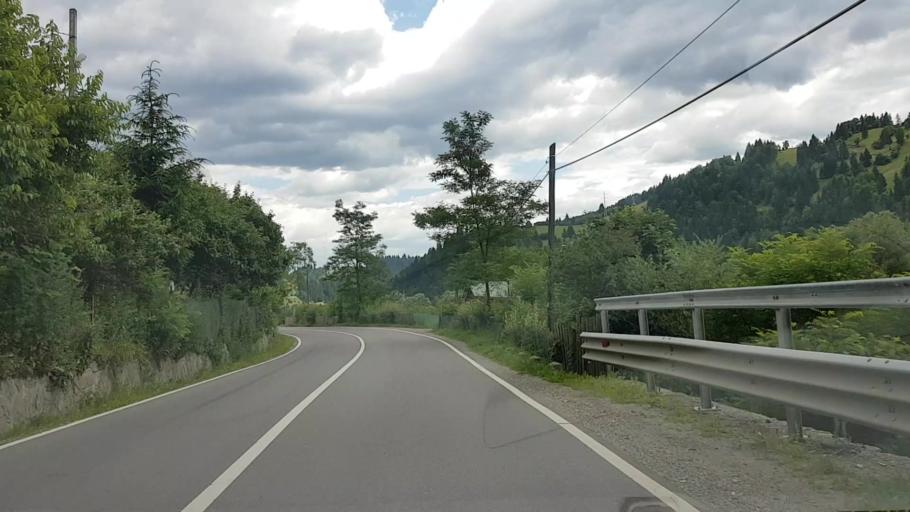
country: RO
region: Neamt
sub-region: Comuna Farcasa
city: Farcasa
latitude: 47.1597
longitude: 25.8231
